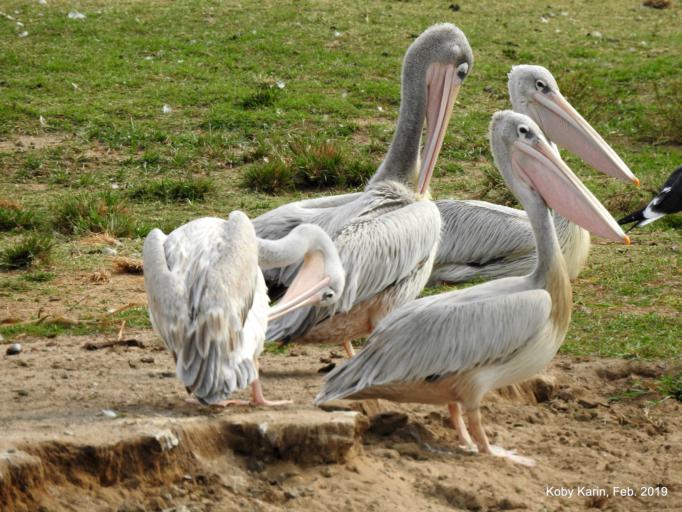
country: UG
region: Western Region
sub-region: Rubirizi District
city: Rubirizi
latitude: -0.2081
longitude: 29.8906
